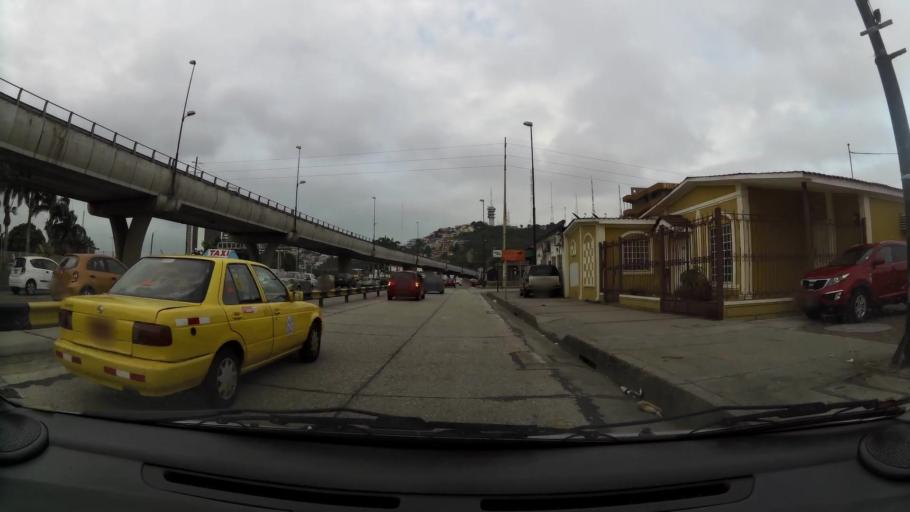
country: EC
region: Guayas
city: Eloy Alfaro
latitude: -2.1732
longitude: -79.8797
